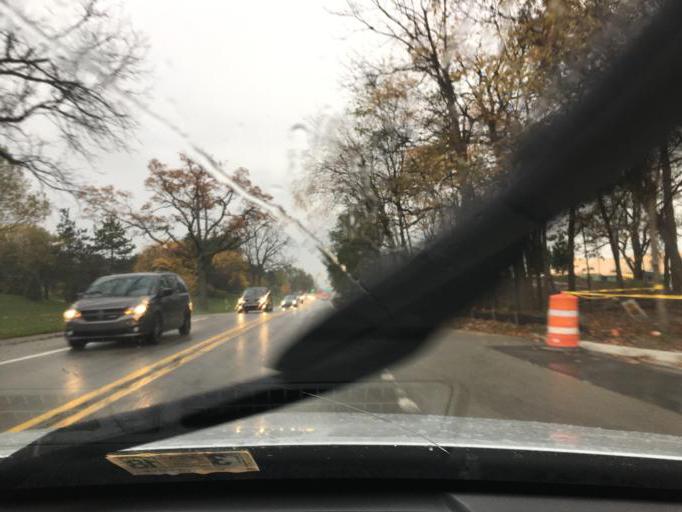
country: US
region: Michigan
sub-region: Oakland County
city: Auburn Hills
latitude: 42.7129
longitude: -83.1957
